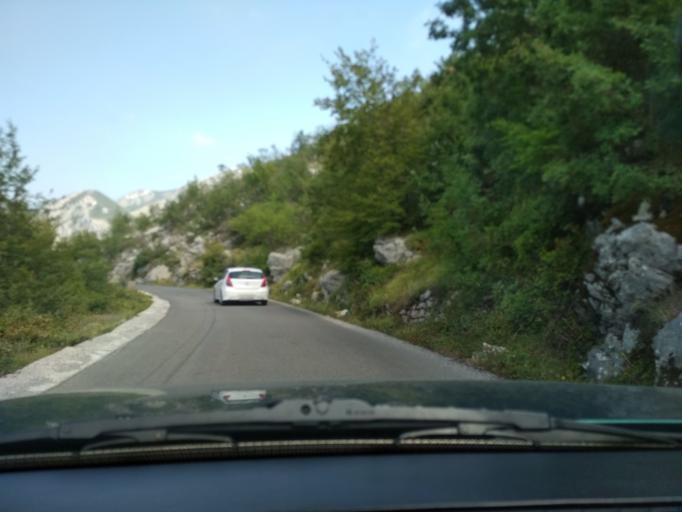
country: ME
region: Kotor
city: Kotor
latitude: 42.4142
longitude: 18.7918
